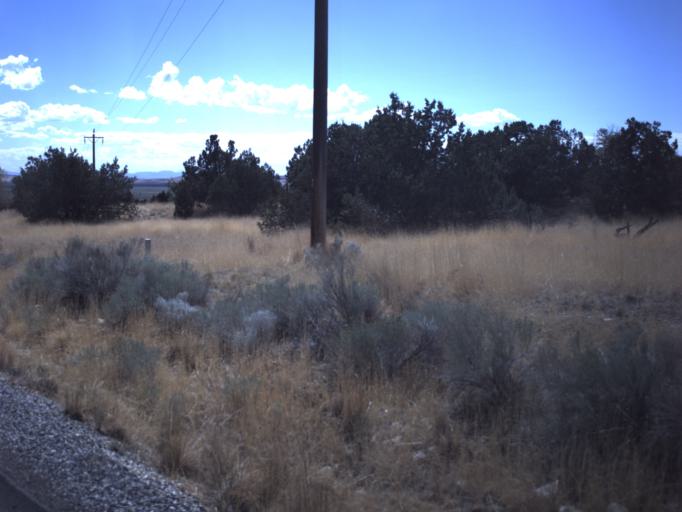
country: US
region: Utah
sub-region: Tooele County
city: Grantsville
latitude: 40.3208
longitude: -112.6271
